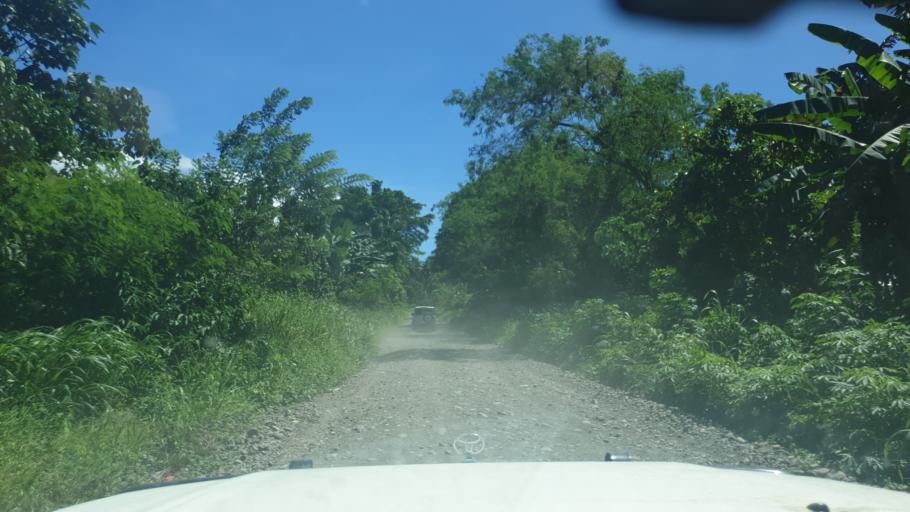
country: PG
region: Bougainville
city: Buka
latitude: -5.6701
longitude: 155.1038
